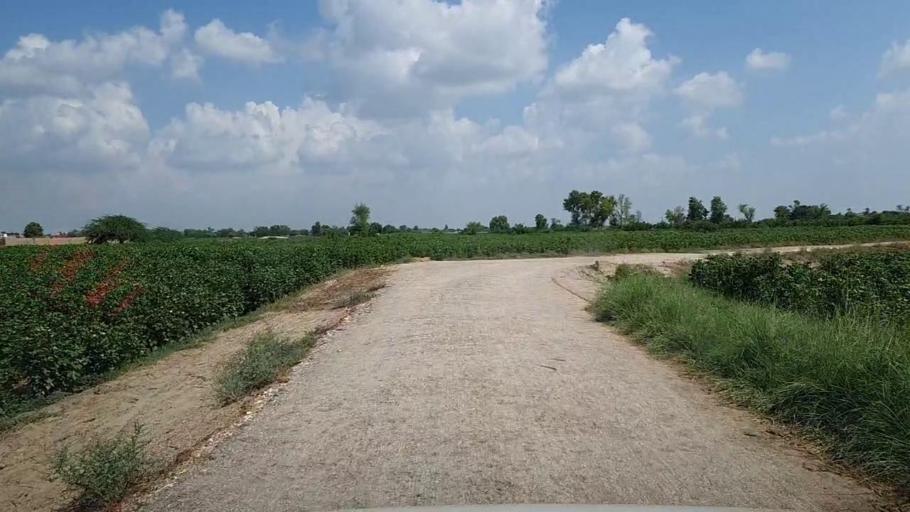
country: PK
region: Sindh
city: Kandiaro
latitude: 27.0017
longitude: 68.3074
